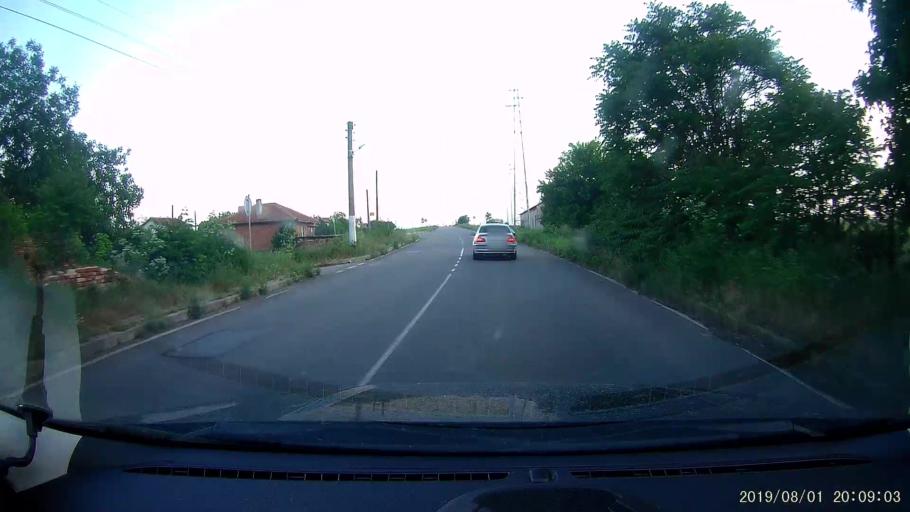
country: BG
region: Yambol
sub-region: Obshtina Yambol
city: Yambol
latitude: 42.5015
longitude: 26.5914
